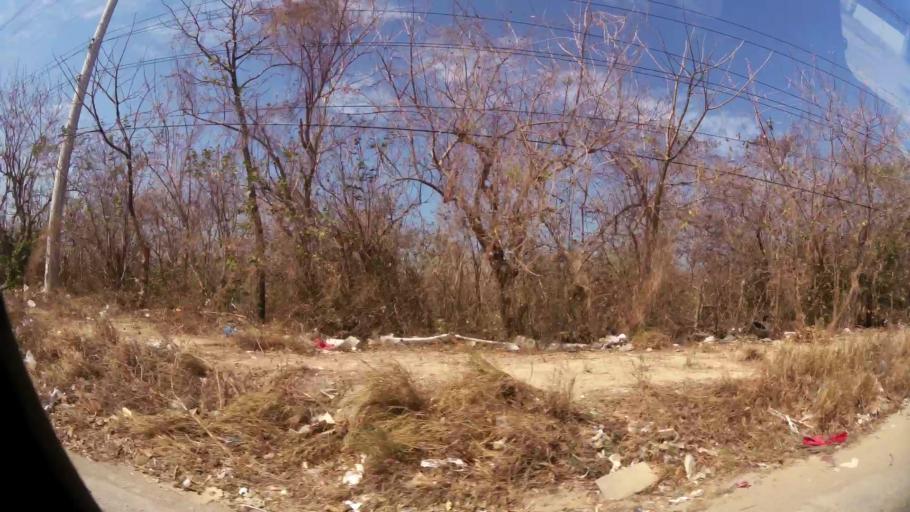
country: CO
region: Atlantico
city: Barranquilla
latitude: 10.9816
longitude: -74.8406
